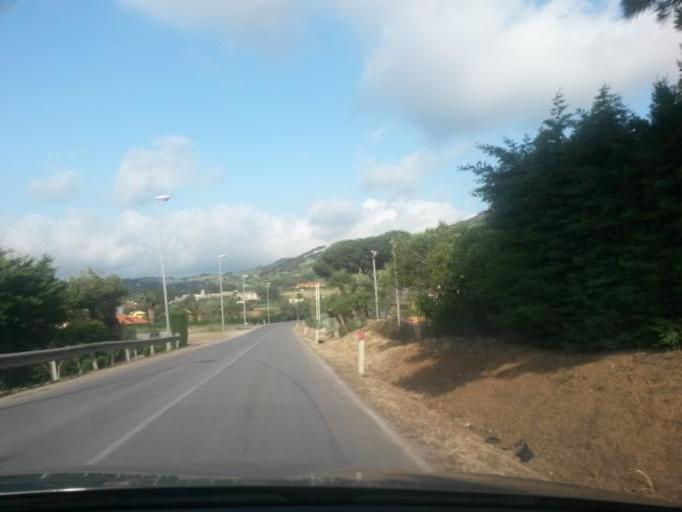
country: IT
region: Tuscany
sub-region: Provincia di Livorno
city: Porto Azzurro
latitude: 42.7741
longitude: 10.4090
